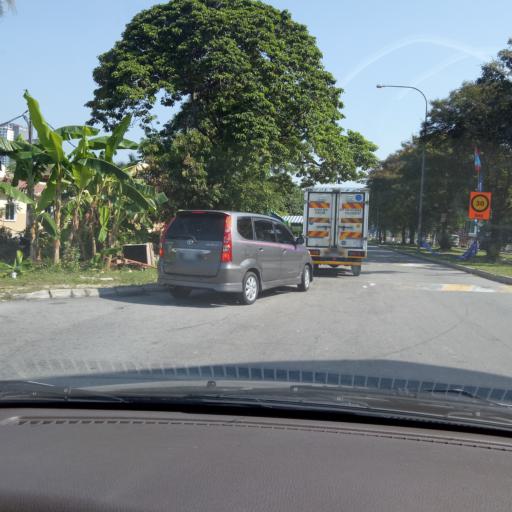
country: MY
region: Selangor
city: Kampong Baharu Balakong
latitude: 3.0260
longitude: 101.7638
